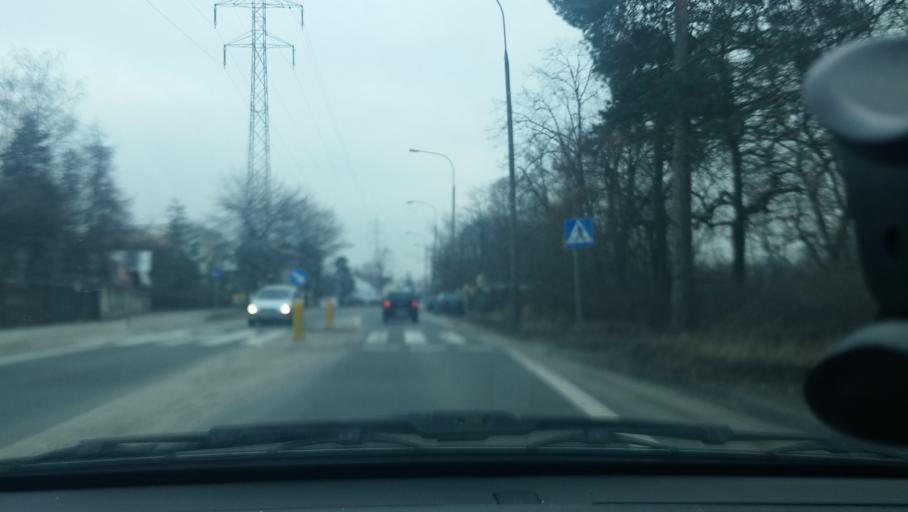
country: PL
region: Masovian Voivodeship
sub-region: Warszawa
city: Wawer
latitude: 52.2200
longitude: 21.1537
